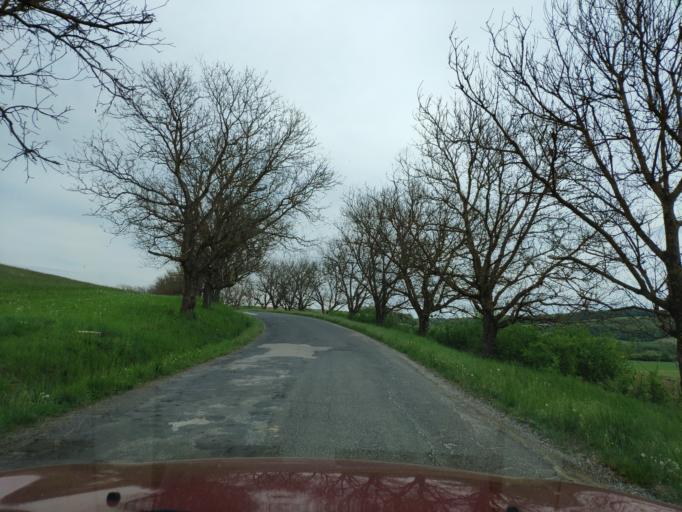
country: SK
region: Banskobystricky
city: Revuca
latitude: 48.4960
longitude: 20.2231
